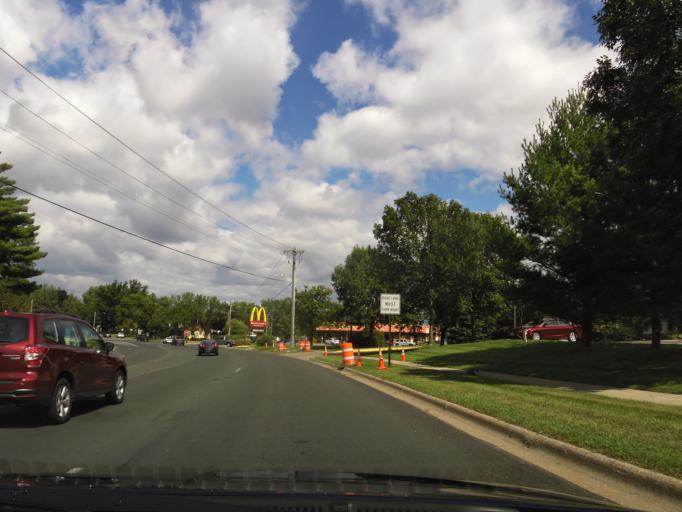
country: US
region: Minnesota
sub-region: Dakota County
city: Inver Grove Heights
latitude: 44.8642
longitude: -93.0428
